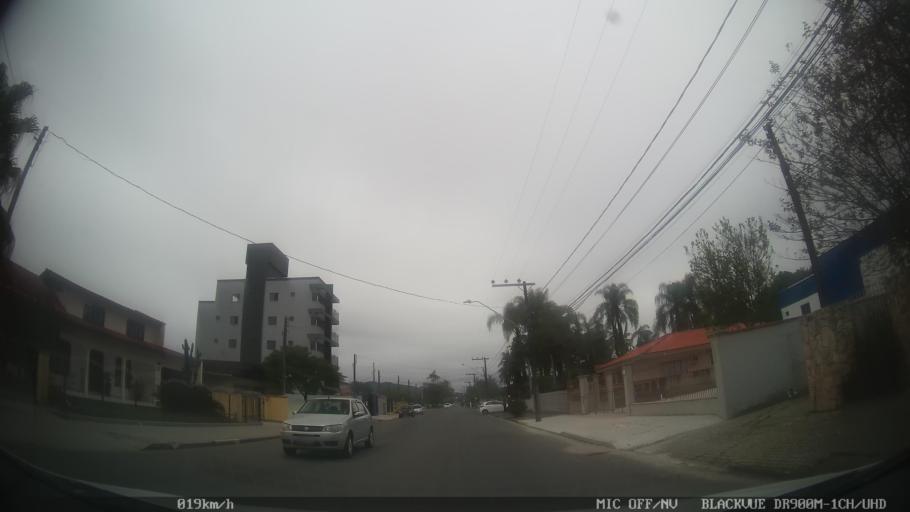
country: BR
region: Santa Catarina
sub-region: Joinville
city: Joinville
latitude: -26.2656
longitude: -48.8162
